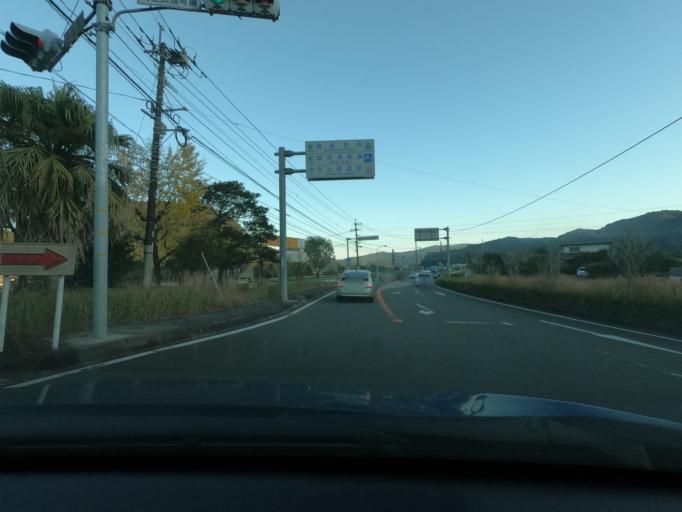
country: JP
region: Kagoshima
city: Satsumasendai
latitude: 31.8039
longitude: 130.3974
